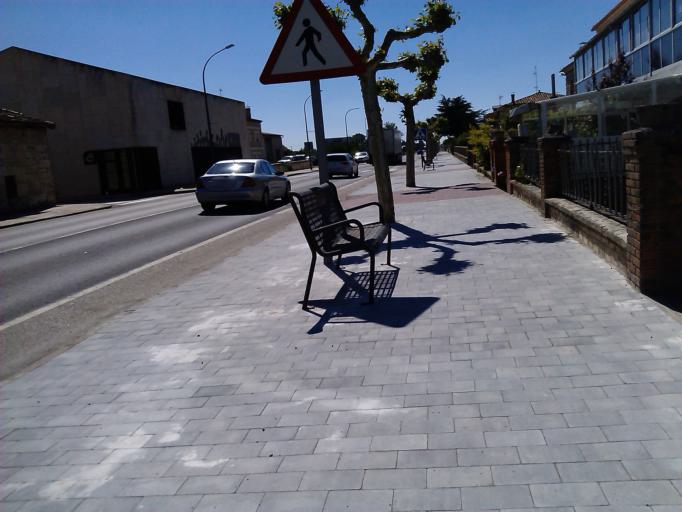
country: ES
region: Castille and Leon
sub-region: Provincia de Burgos
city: Ibeas de Juarros
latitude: 42.3319
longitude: -3.5370
